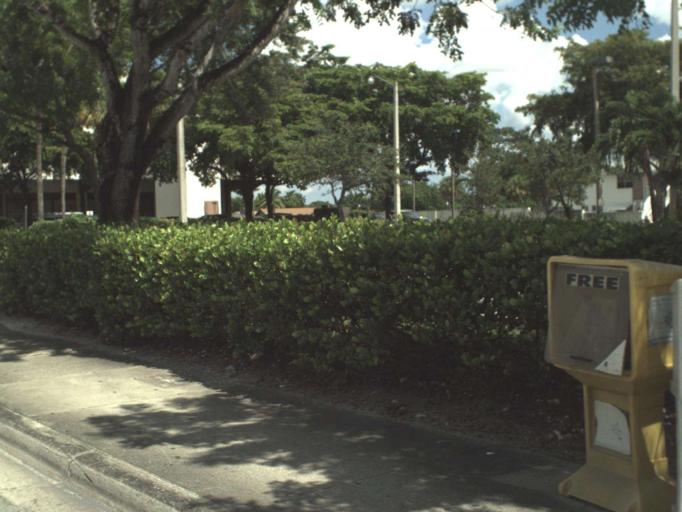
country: US
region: Florida
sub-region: Miami-Dade County
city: Andover
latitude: 25.9626
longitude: -80.2057
